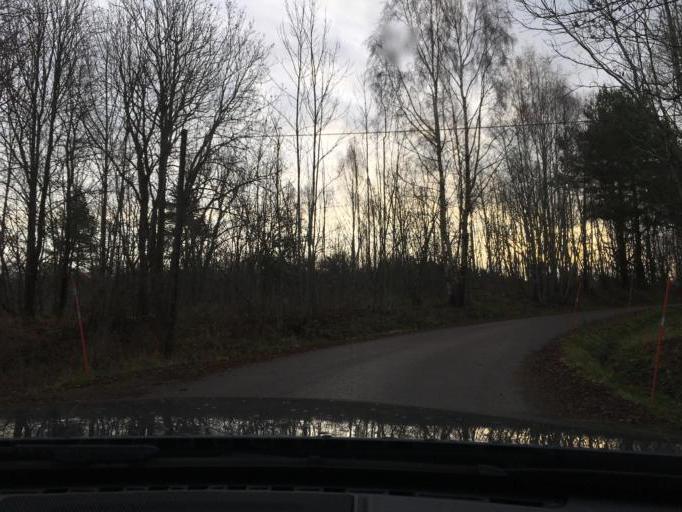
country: SE
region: Joenkoeping
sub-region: Jonkopings Kommun
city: Graenna
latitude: 57.9945
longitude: 14.4290
